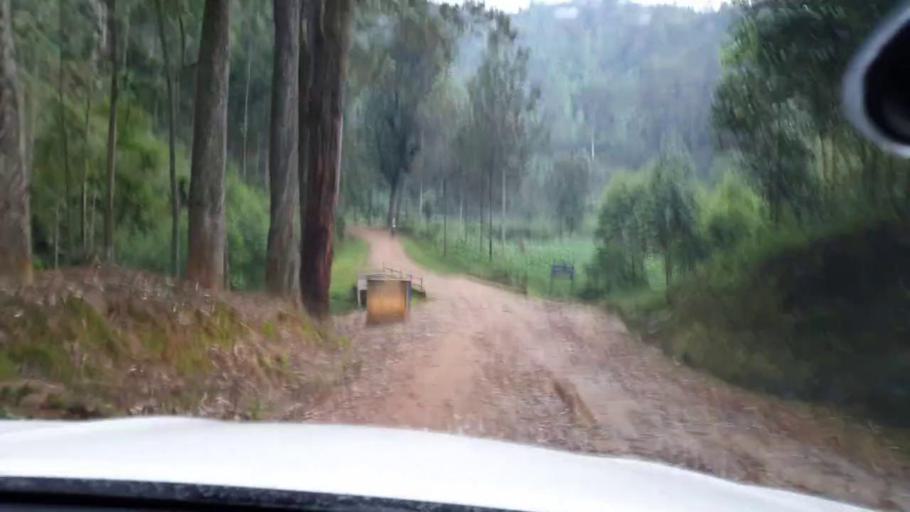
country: RW
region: Western Province
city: Cyangugu
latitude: -2.4111
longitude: 29.1932
